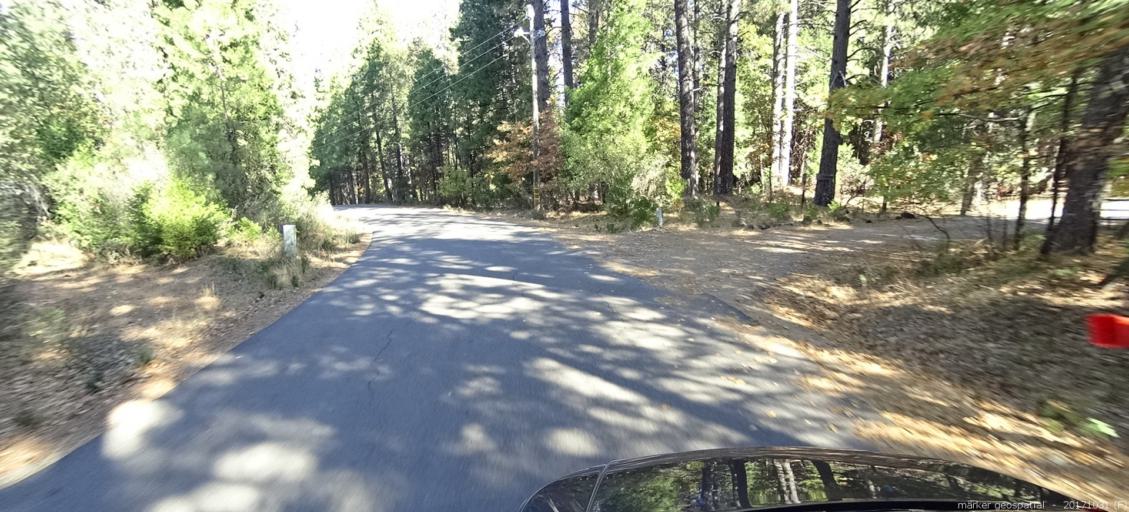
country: US
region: California
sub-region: Shasta County
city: Shingletown
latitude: 40.5184
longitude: -121.9323
